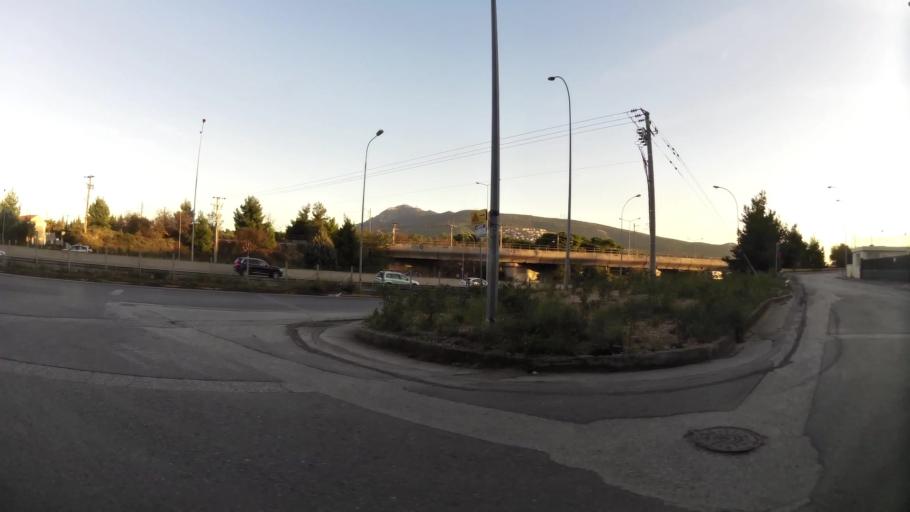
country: GR
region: Attica
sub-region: Nomarchia Anatolikis Attikis
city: Kryoneri
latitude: 38.1267
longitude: 23.8364
